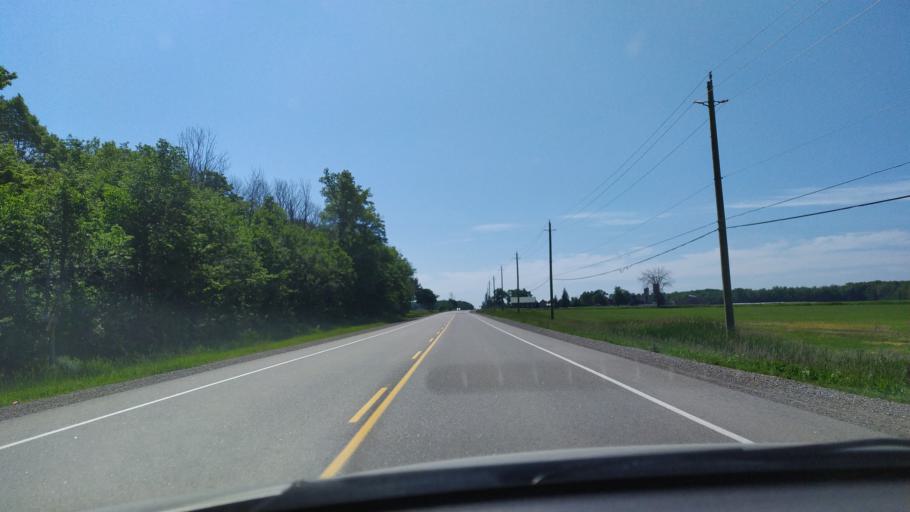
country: CA
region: Ontario
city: Stratford
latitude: 43.4587
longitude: -80.7611
